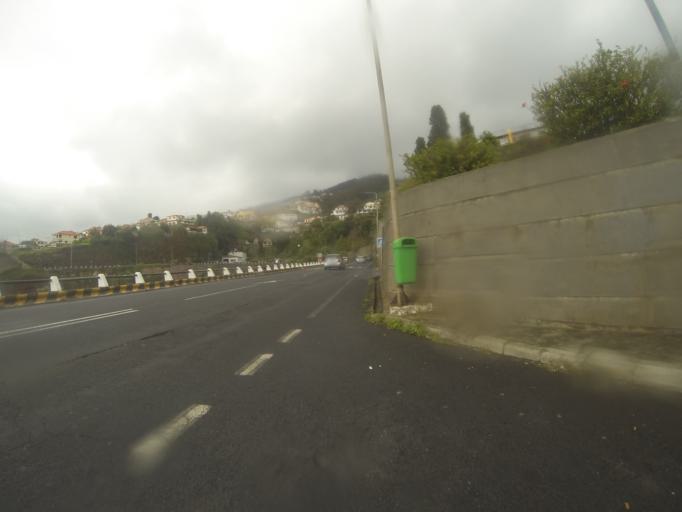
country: PT
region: Madeira
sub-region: Funchal
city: Nossa Senhora do Monte
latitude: 32.6565
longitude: -16.8832
